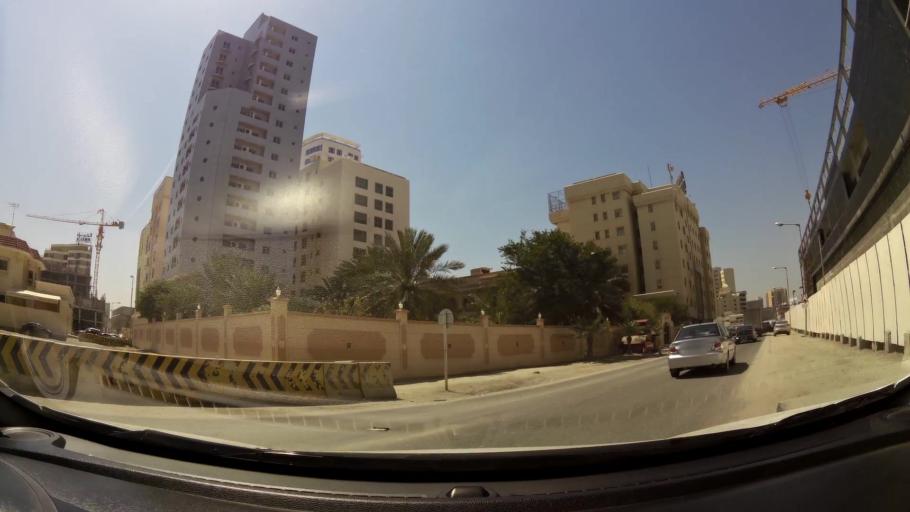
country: BH
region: Manama
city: Manama
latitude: 26.2154
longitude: 50.6029
